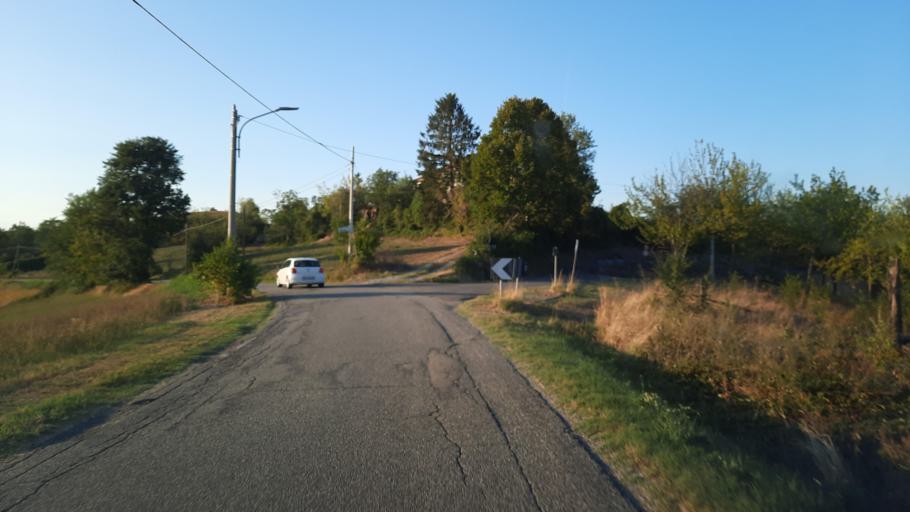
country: IT
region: Piedmont
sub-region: Provincia di Alessandria
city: Cereseto
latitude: 45.0742
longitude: 8.3282
